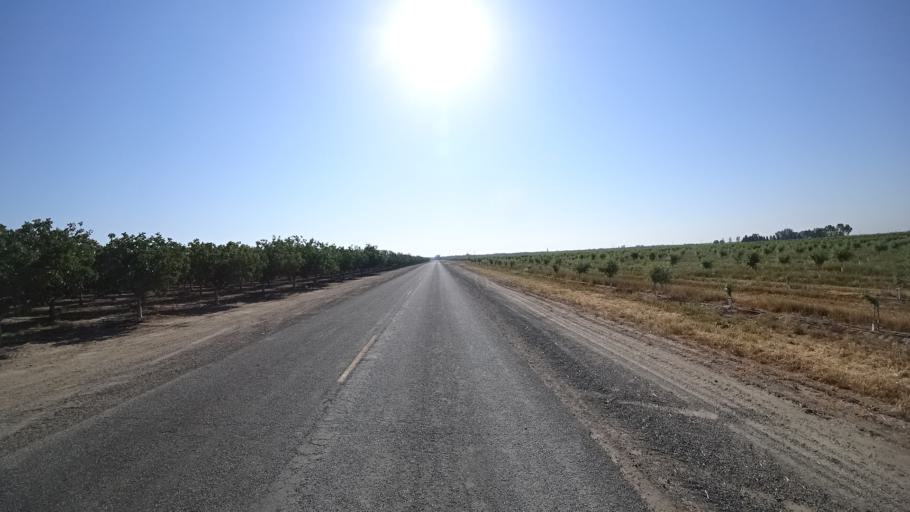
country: US
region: California
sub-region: Kings County
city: Lucerne
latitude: 36.3935
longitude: -119.6792
